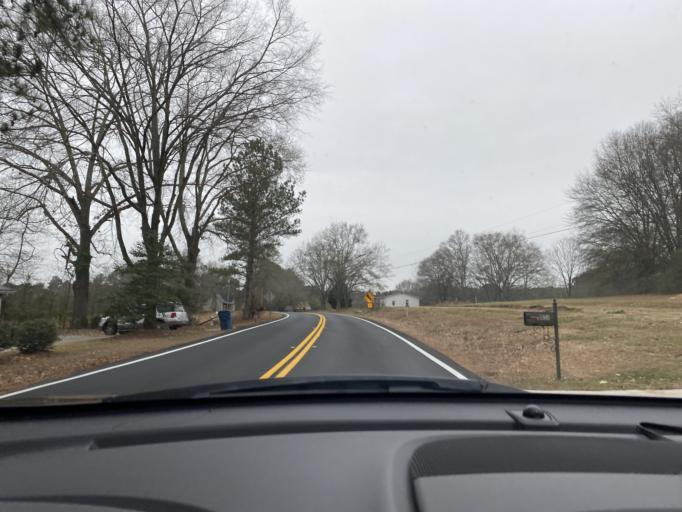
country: US
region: Georgia
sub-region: Gwinnett County
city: Grayson
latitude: 33.9220
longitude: -83.9177
